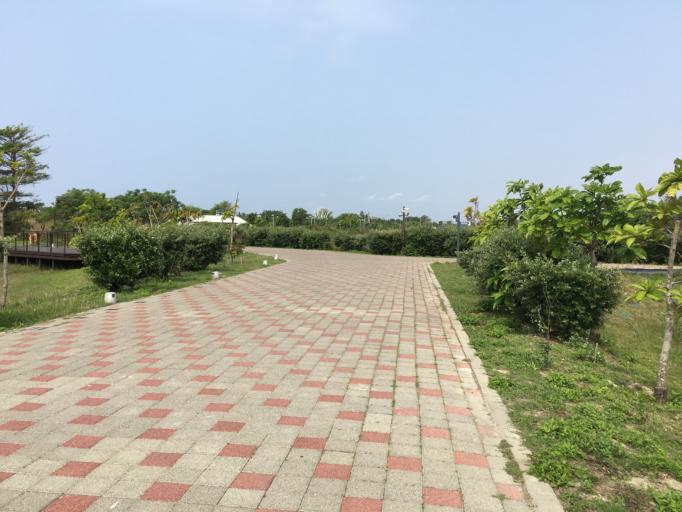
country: TW
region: Taiwan
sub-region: Tainan
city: Tainan
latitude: 23.0026
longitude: 120.1381
